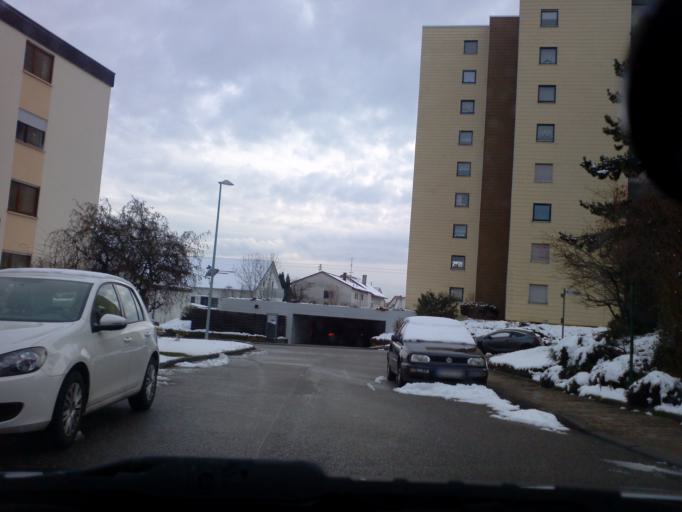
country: DE
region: Baden-Wuerttemberg
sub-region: Regierungsbezirk Stuttgart
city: Walheim
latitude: 49.0157
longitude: 9.1530
